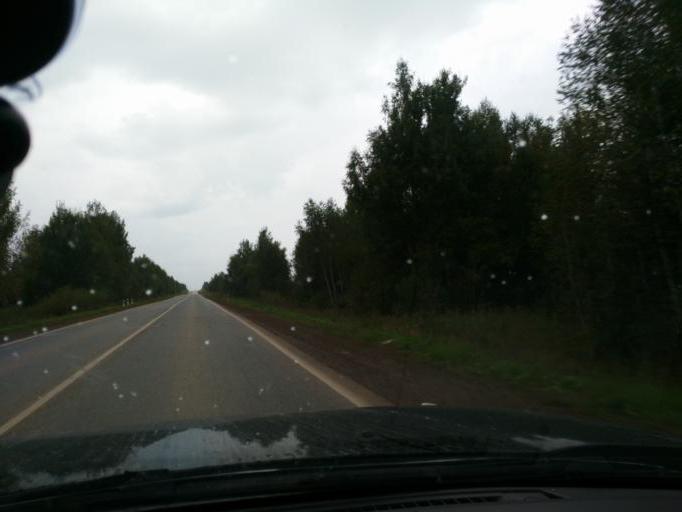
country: RU
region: Perm
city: Barda
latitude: 56.8643
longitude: 55.9049
